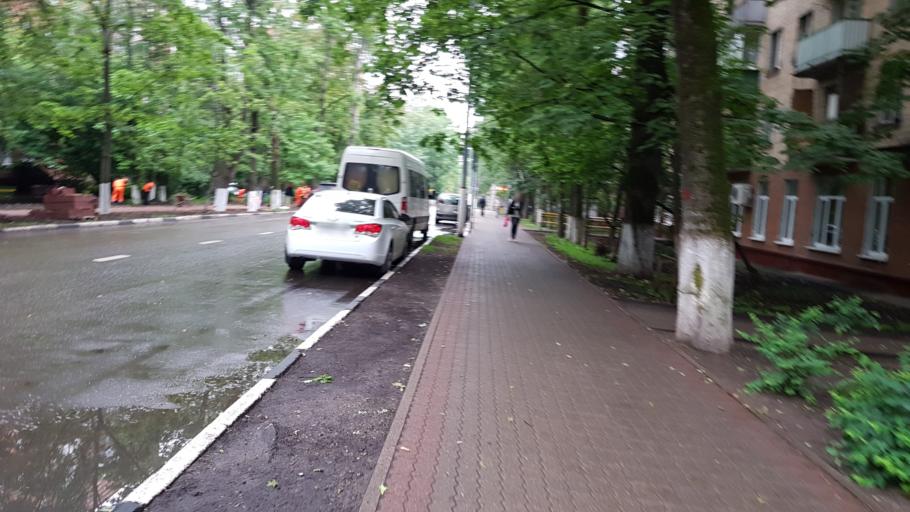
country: RU
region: Moscow
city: Khimki
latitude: 55.8903
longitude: 37.4516
